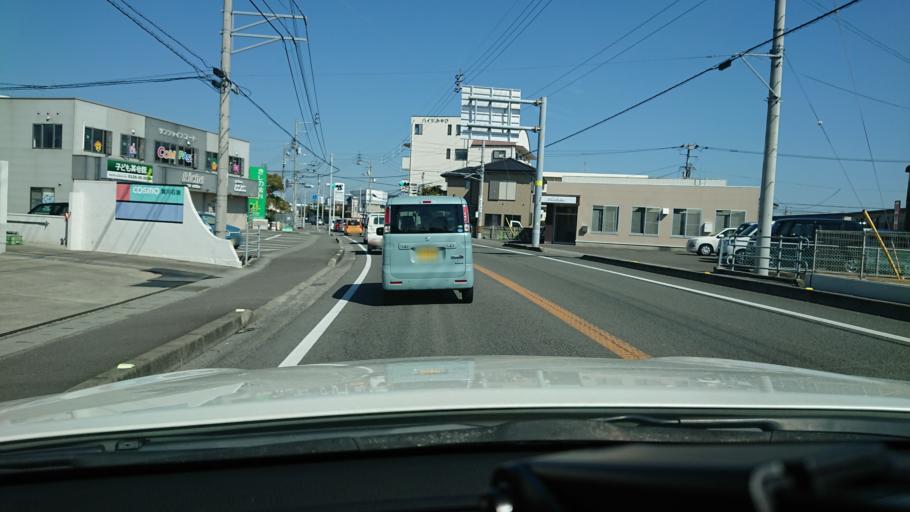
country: JP
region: Tokushima
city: Narutocho-mitsuishi
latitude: 34.1423
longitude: 134.5932
